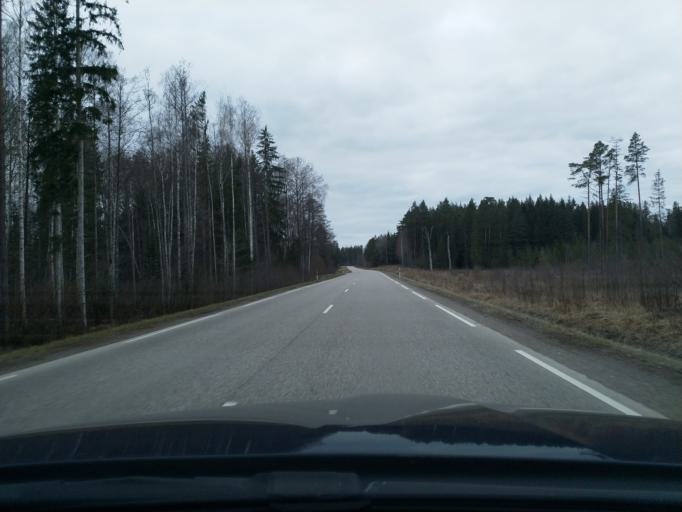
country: LV
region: Kuldigas Rajons
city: Kuldiga
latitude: 56.9539
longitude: 22.1454
